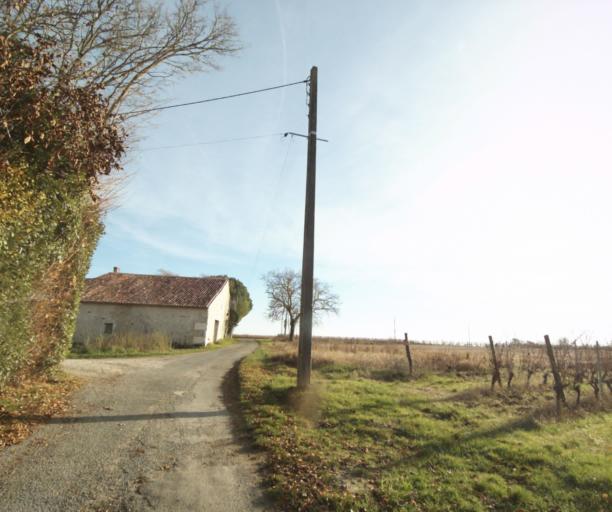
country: FR
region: Poitou-Charentes
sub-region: Departement de la Charente-Maritime
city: Chaniers
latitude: 45.7345
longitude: -0.5164
